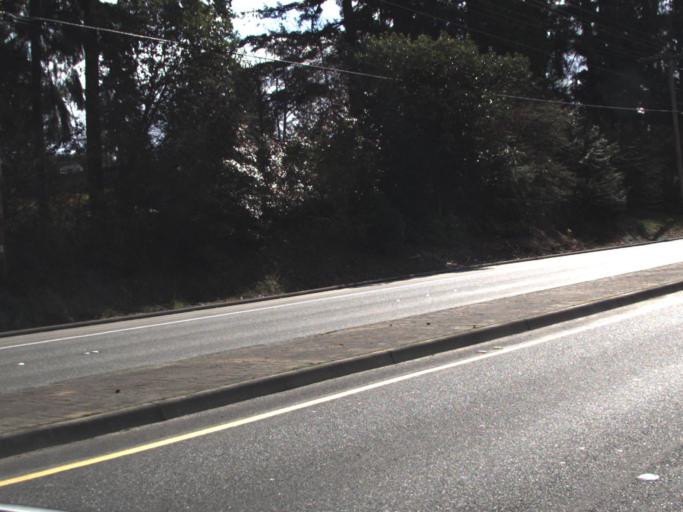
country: US
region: Washington
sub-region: King County
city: Lakeland South
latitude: 47.2767
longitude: -122.3089
